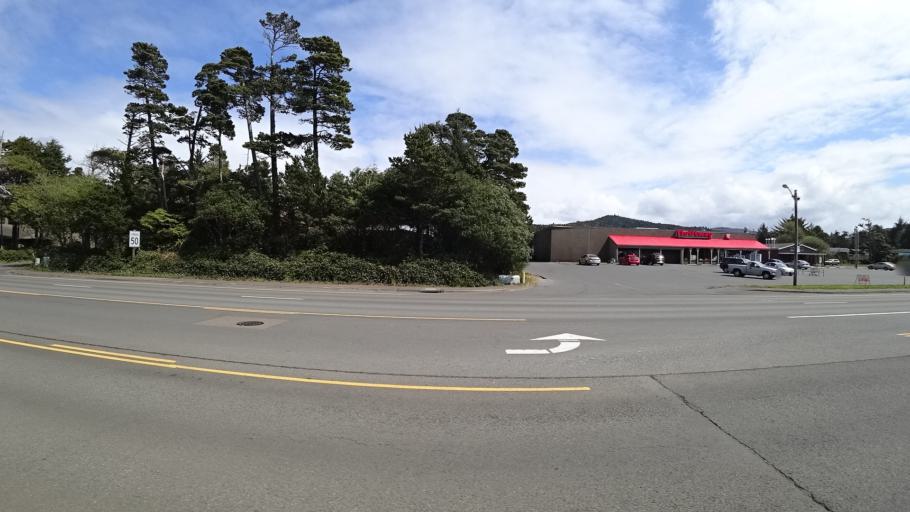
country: US
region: Oregon
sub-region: Lincoln County
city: Lincoln Beach
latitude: 44.8504
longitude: -124.0441
